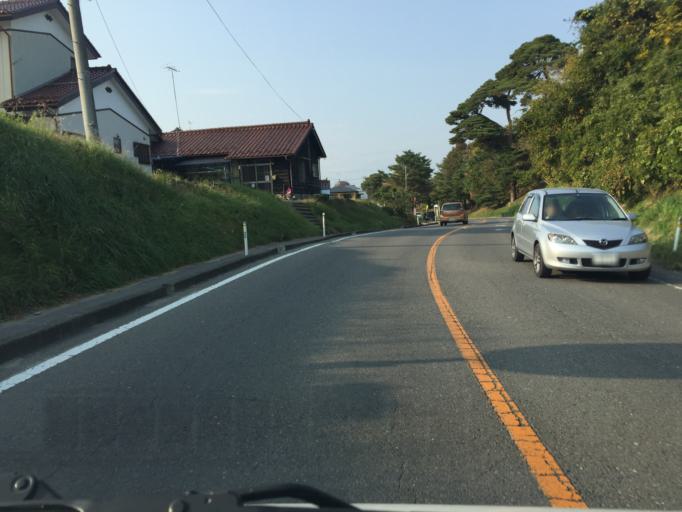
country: JP
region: Fukushima
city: Koriyama
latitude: 37.4316
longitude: 140.3918
